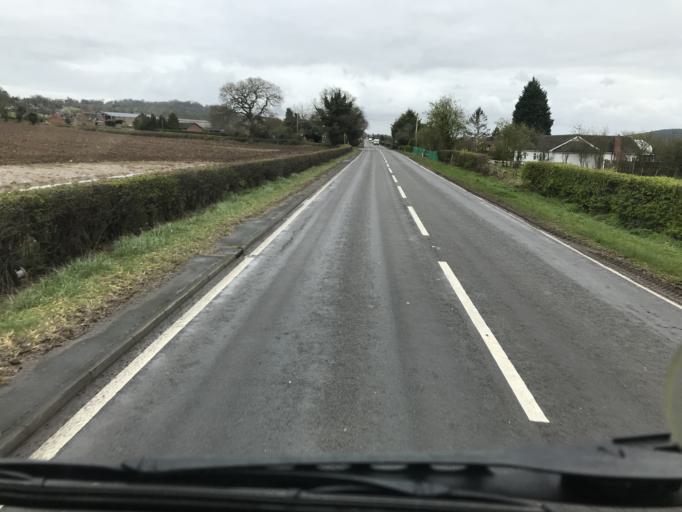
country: GB
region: England
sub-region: Cheshire West and Chester
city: Tattenhall
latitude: 53.0963
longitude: -2.7763
